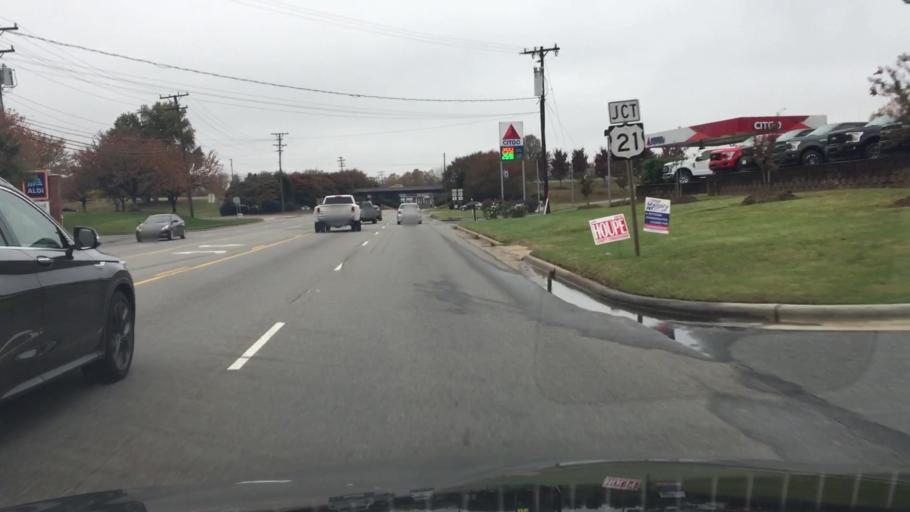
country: US
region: North Carolina
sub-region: Iredell County
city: Mooresville
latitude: 35.5888
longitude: -80.8348
